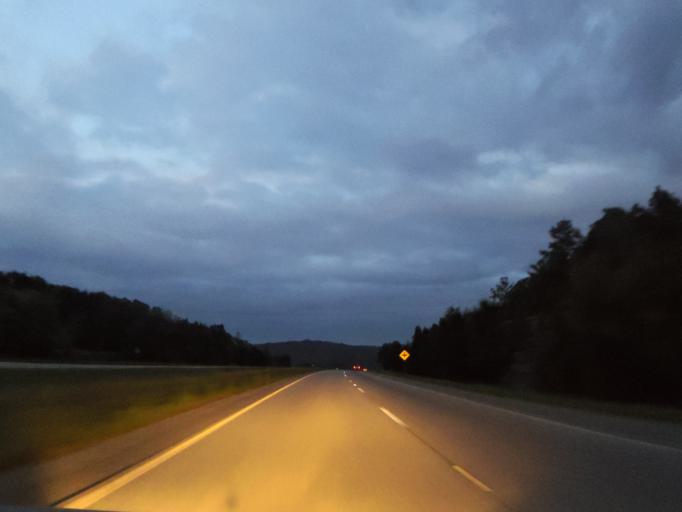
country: US
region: Alabama
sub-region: Madison County
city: New Hope
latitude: 34.6135
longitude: -86.2393
